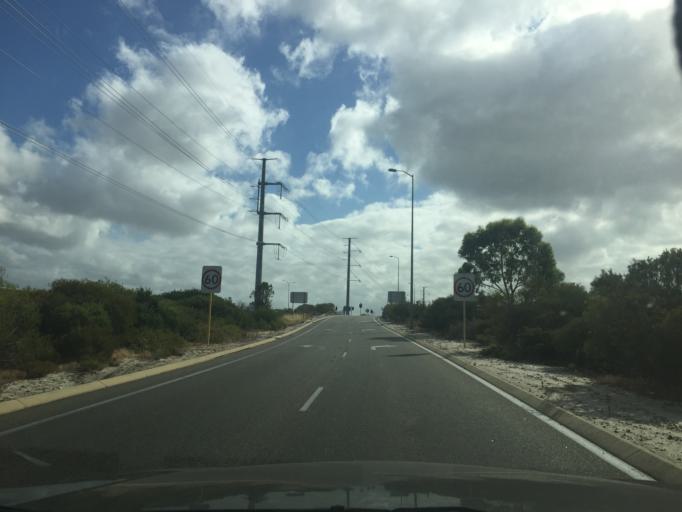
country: AU
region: Western Australia
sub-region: Canning
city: Canning Vale
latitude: -32.0566
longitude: 115.9064
